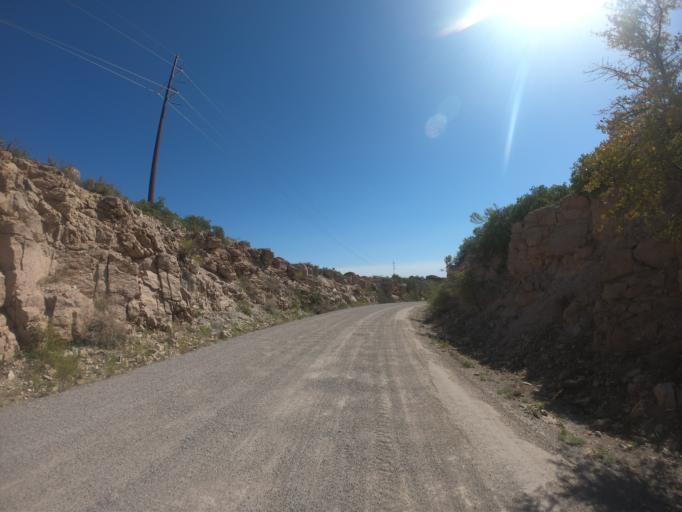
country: US
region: Arizona
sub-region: Pinal County
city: Superior
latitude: 33.3281
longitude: -111.0382
